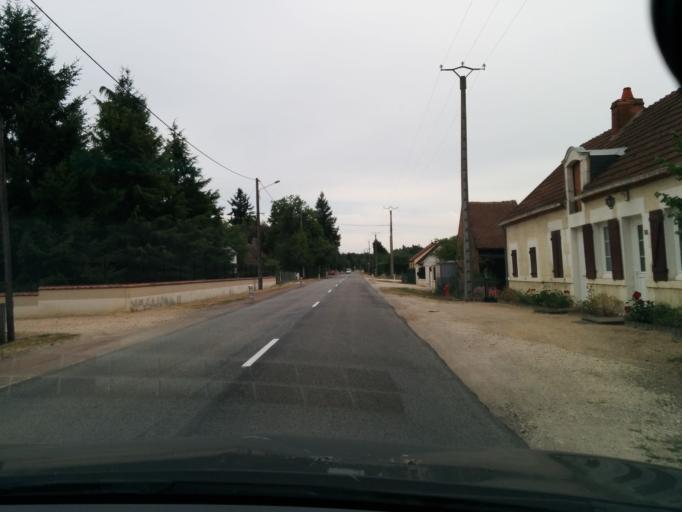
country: FR
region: Centre
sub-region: Departement du Loiret
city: Tigy
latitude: 47.7918
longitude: 2.1984
